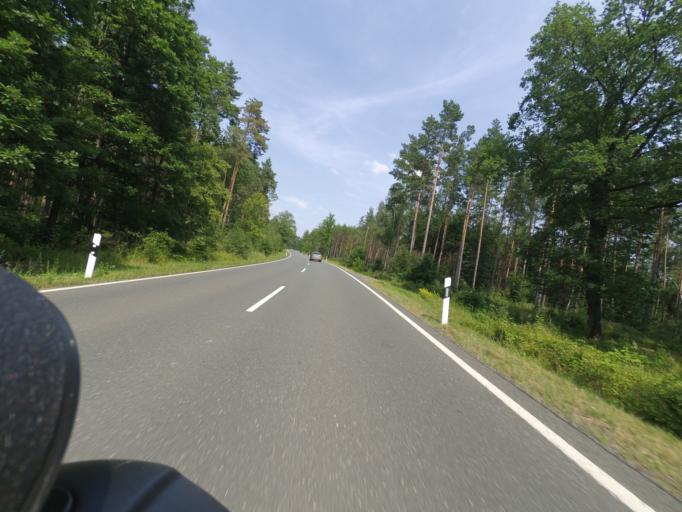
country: DE
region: Thuringia
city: Rauda
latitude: 50.9240
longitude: 11.9462
